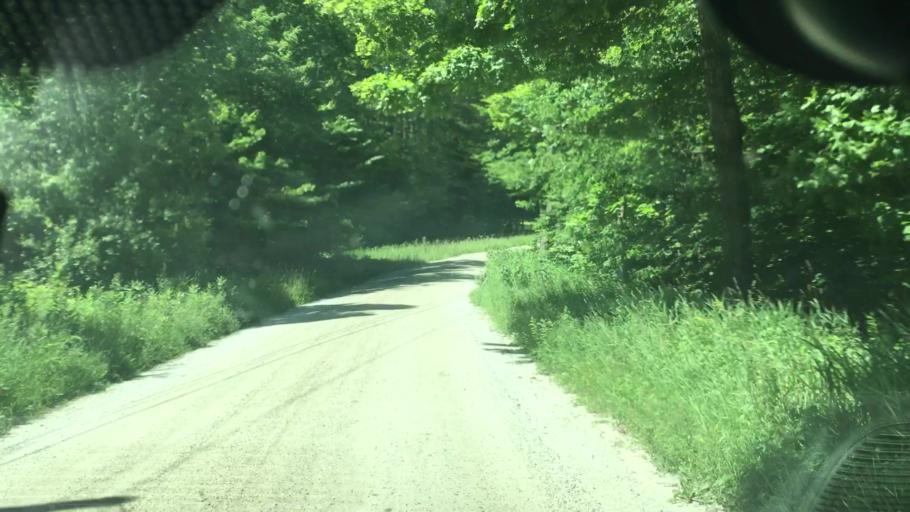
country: US
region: Vermont
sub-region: Windsor County
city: Chester
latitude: 43.4295
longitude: -72.7029
